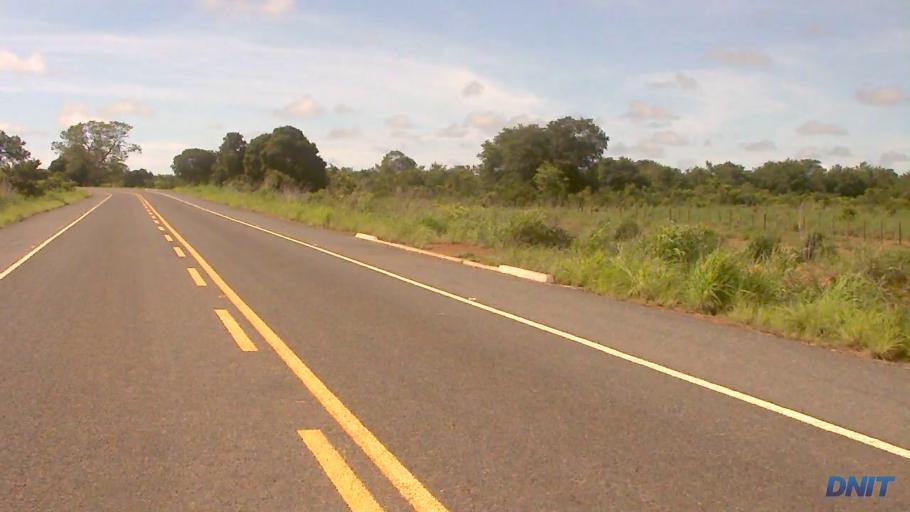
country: BR
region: Goias
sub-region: Sao Miguel Do Araguaia
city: Sao Miguel do Araguaia
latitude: -13.3105
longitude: -50.1717
